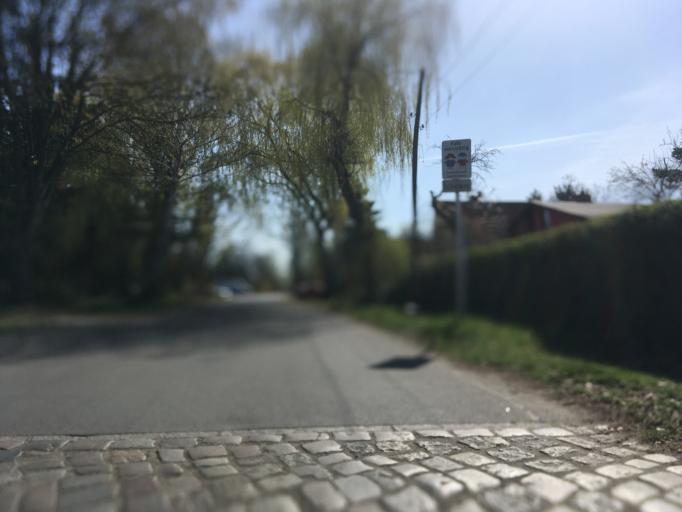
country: DE
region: Berlin
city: Kaulsdorf
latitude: 52.5074
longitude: 13.5973
